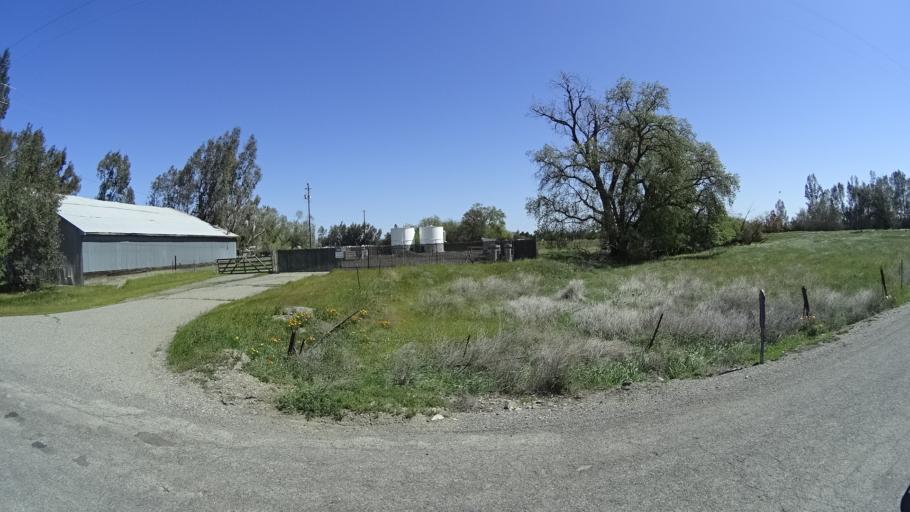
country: US
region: California
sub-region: Glenn County
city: Orland
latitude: 39.7750
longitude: -122.2386
